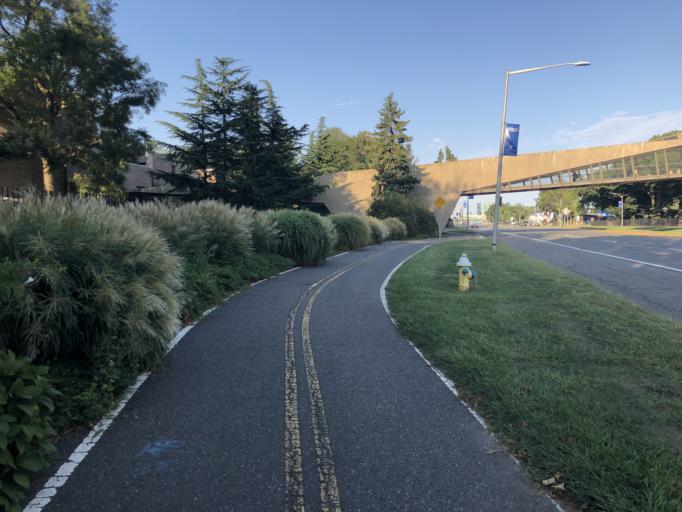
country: US
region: New York
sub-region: Nassau County
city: East Garden City
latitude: 40.7153
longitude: -73.6015
